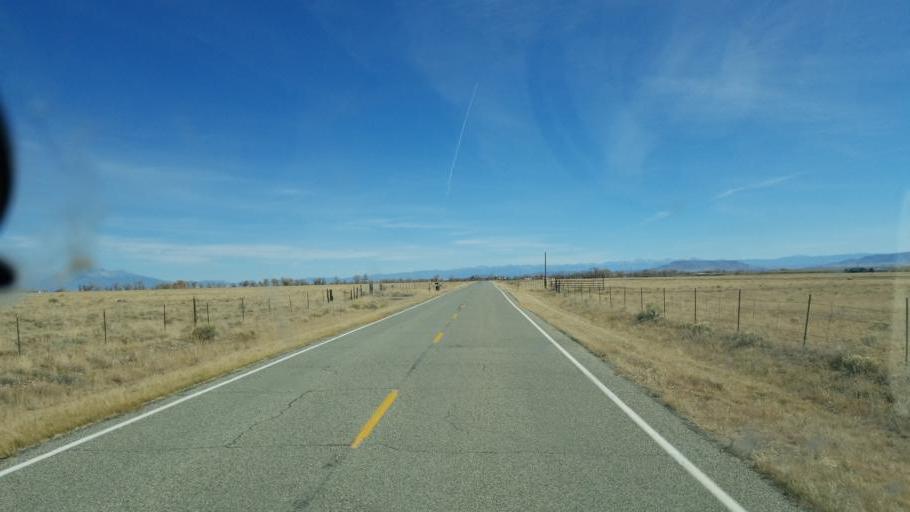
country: US
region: Colorado
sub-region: Conejos County
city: Conejos
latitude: 37.2834
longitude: -106.1351
